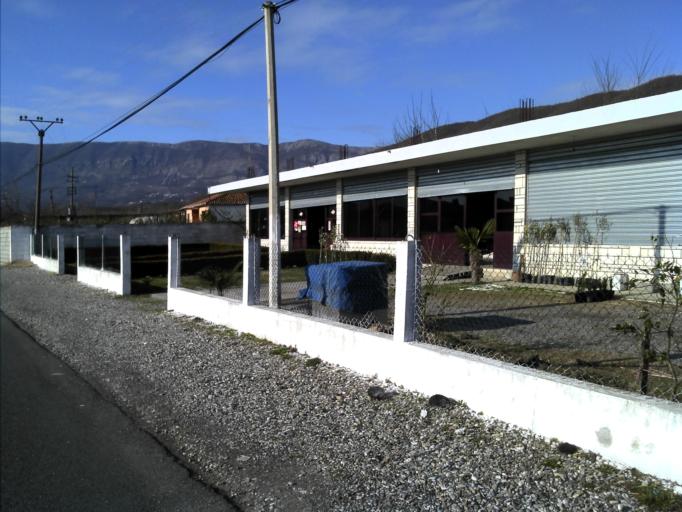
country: AL
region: Shkoder
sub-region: Rrethi i Shkodres
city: Dajc
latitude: 42.0200
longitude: 19.3823
